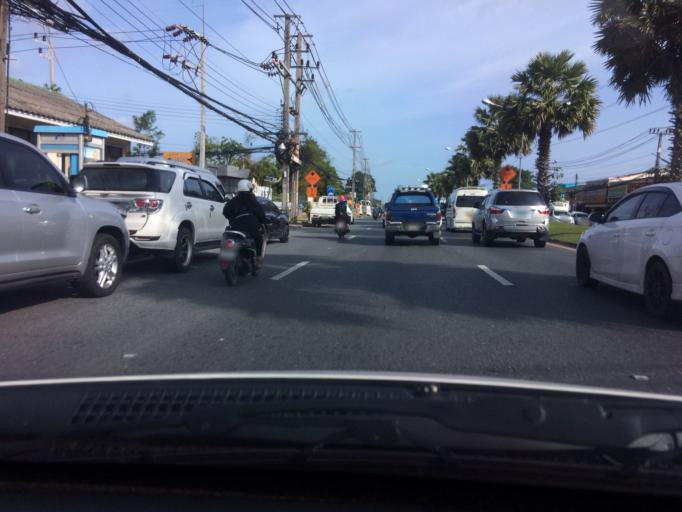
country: TH
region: Phuket
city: Ban Ko Kaeo
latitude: 7.9640
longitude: 98.3772
